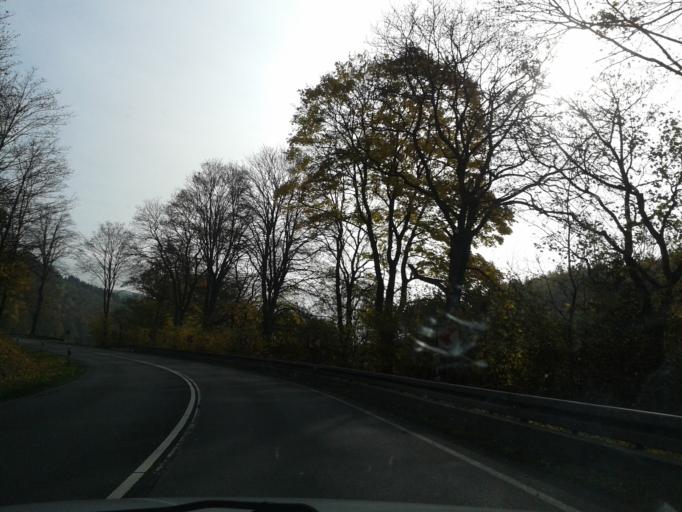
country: DE
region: North Rhine-Westphalia
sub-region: Regierungsbezirk Arnsberg
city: Olsberg
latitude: 51.3241
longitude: 8.4954
